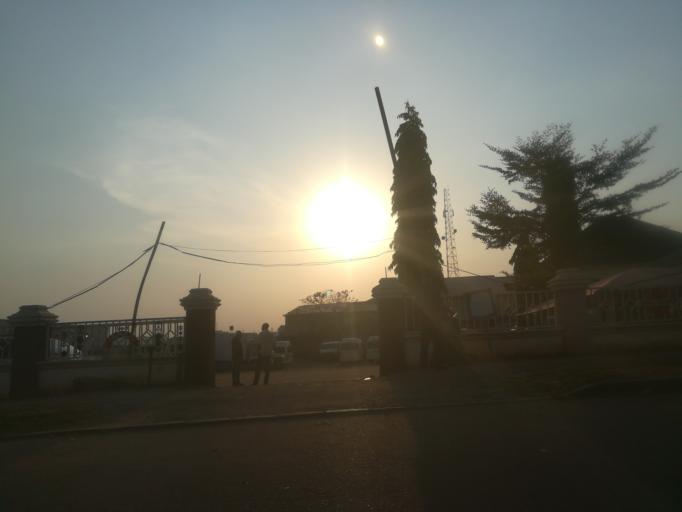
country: NG
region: Abuja Federal Capital Territory
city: Abuja
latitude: 9.0654
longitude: 7.4401
